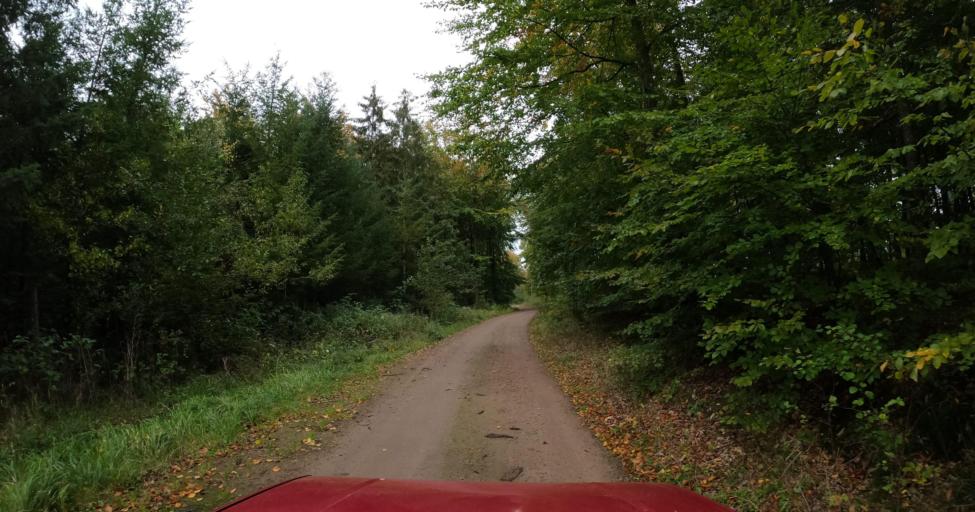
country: PL
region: West Pomeranian Voivodeship
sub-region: Powiat koszalinski
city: Polanow
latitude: 54.1157
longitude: 16.5223
